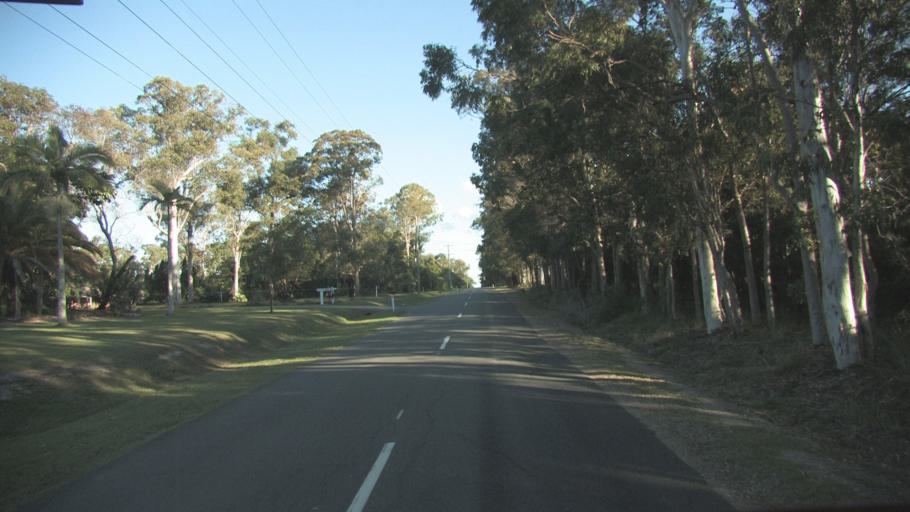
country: AU
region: Queensland
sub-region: Redland
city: Redland Bay
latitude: -27.6770
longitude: 153.2758
